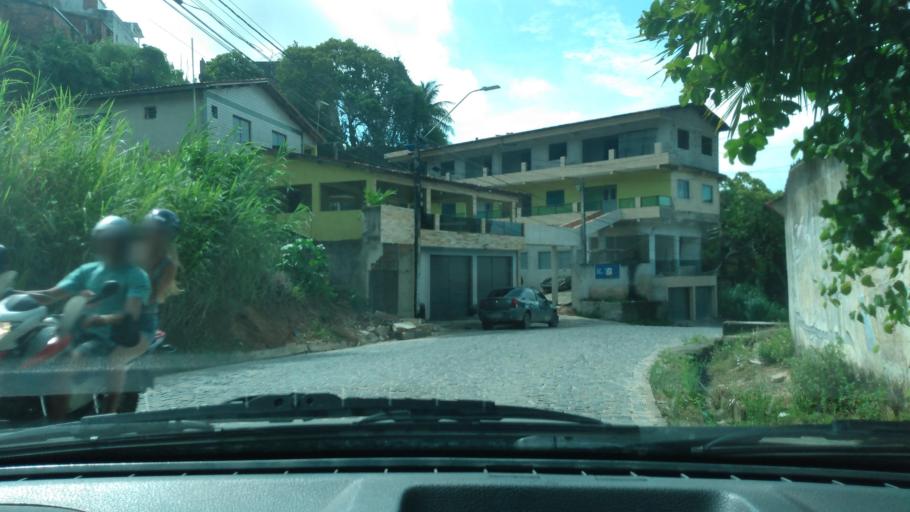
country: BR
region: Pernambuco
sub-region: Cabo De Santo Agostinho
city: Cabo
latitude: -8.3436
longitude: -34.9567
